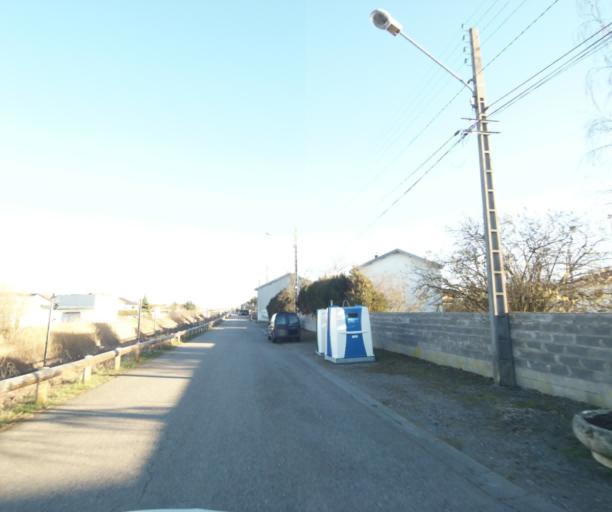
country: FR
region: Lorraine
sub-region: Departement de Meurthe-et-Moselle
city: Laneuveville-devant-Nancy
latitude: 48.6537
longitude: 6.2302
